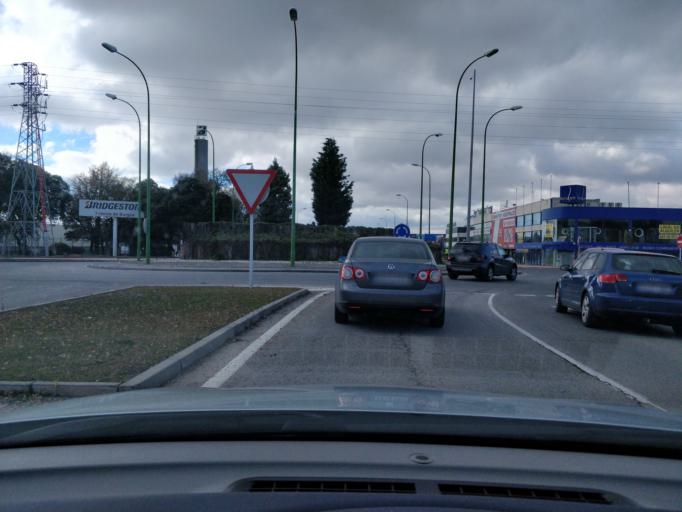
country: ES
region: Castille and Leon
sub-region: Provincia de Burgos
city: Burgos
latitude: 42.3586
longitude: -3.6507
